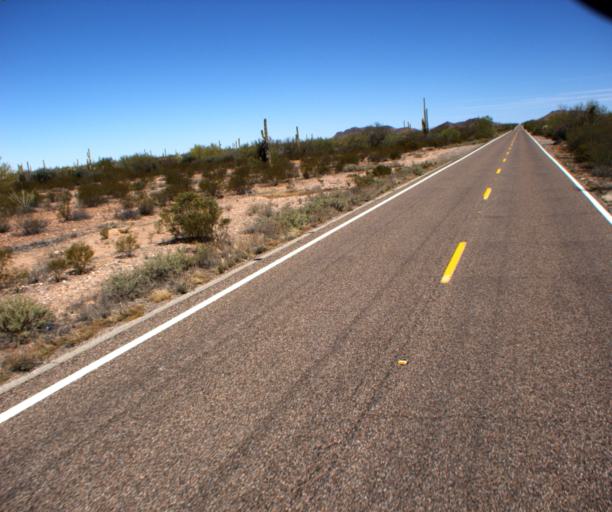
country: MX
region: Sonora
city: Sonoyta
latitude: 32.0498
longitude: -112.7915
